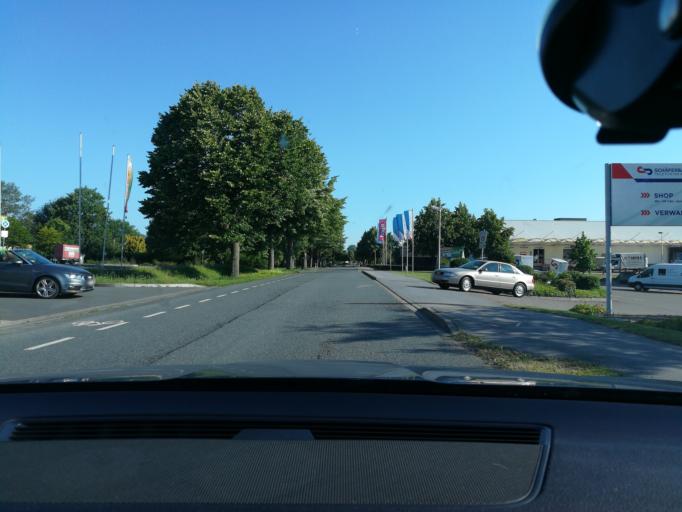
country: DE
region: North Rhine-Westphalia
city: Porta Westfalica
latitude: 52.2574
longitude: 8.8989
